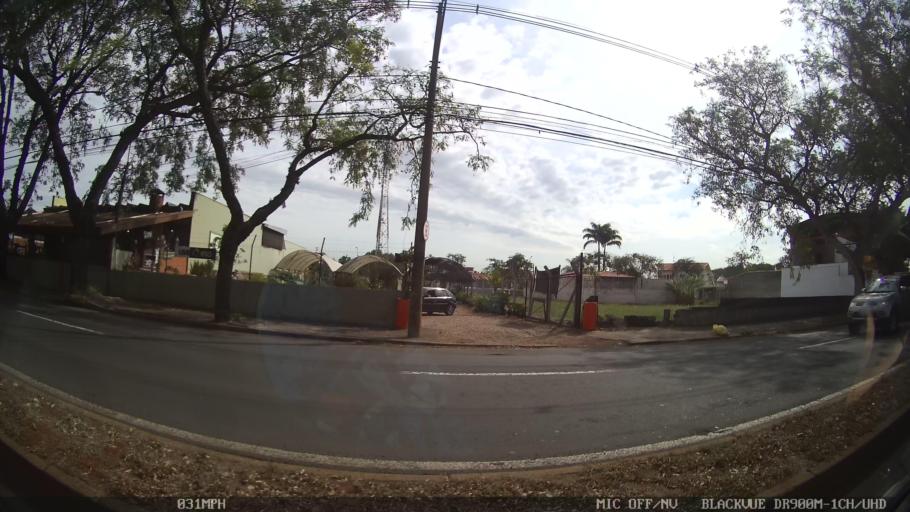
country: BR
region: Sao Paulo
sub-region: Piracicaba
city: Piracicaba
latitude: -22.7188
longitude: -47.6624
